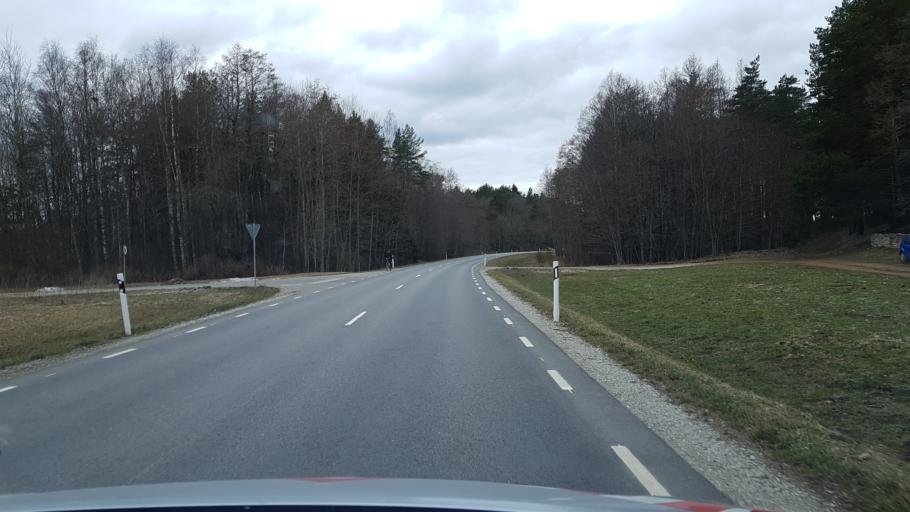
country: EE
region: Ida-Virumaa
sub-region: Narva-Joesuu linn
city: Narva-Joesuu
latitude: 59.4144
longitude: 28.0888
